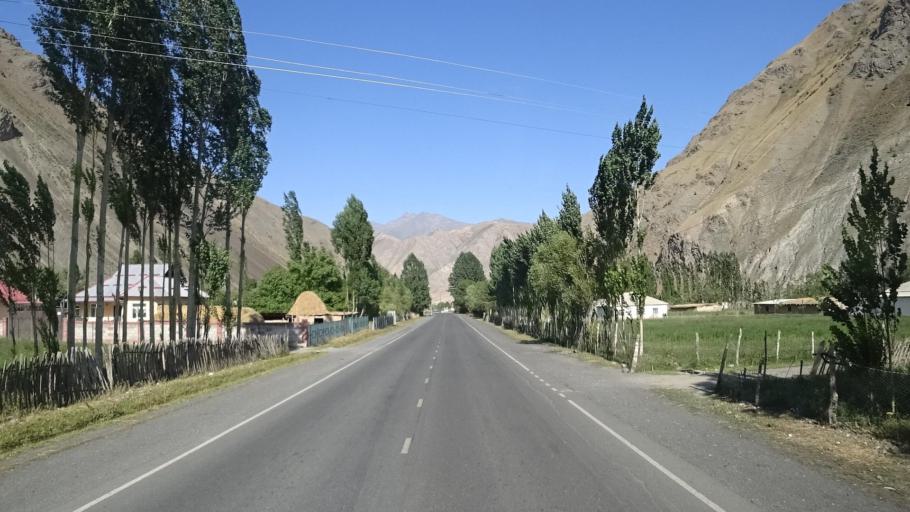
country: KG
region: Osh
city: Gul'cha
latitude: 40.0283
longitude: 73.5050
